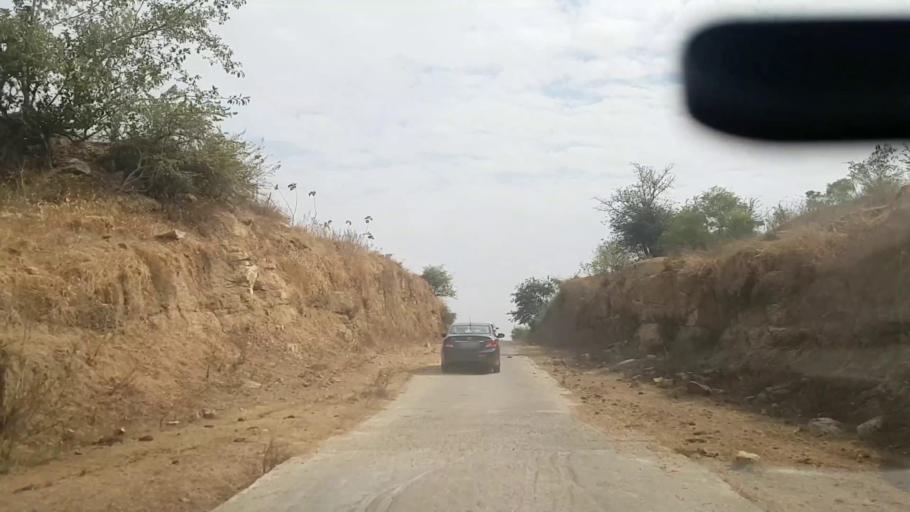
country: IN
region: Telangana
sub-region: Rangareddi
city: Lal Bahadur Nagar
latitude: 17.1772
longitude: 78.7760
